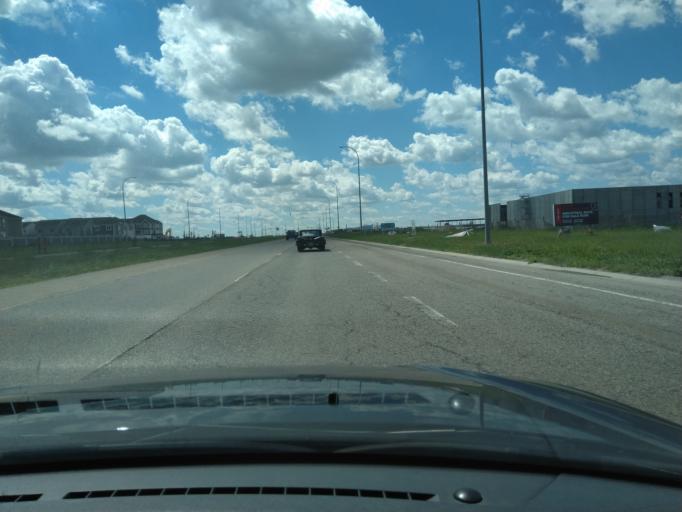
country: CA
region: Alberta
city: Calgary
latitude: 51.1511
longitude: -113.9702
